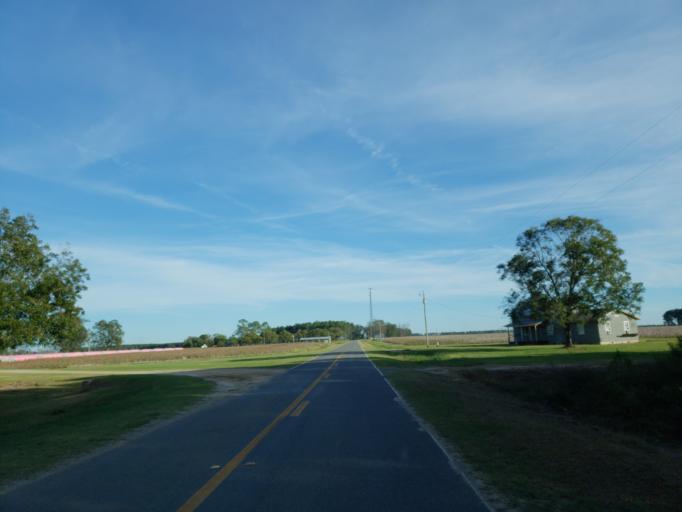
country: US
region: Georgia
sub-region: Dooly County
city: Vienna
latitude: 32.0754
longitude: -83.7847
